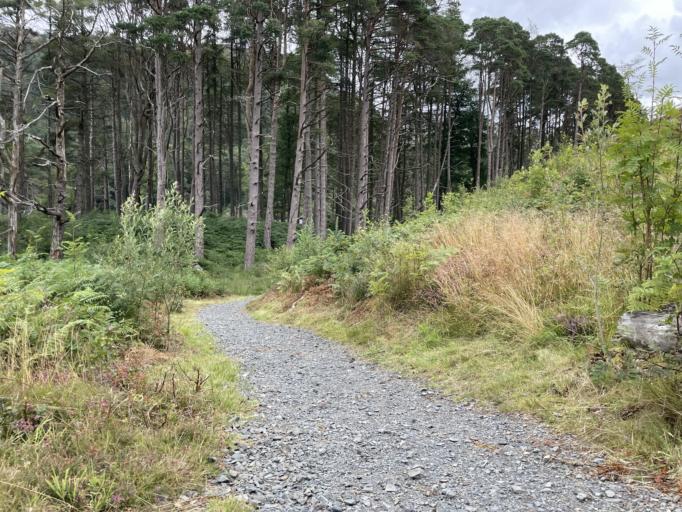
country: GB
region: Scotland
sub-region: Dumfries and Galloway
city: Newton Stewart
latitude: 55.0869
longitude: -4.4944
